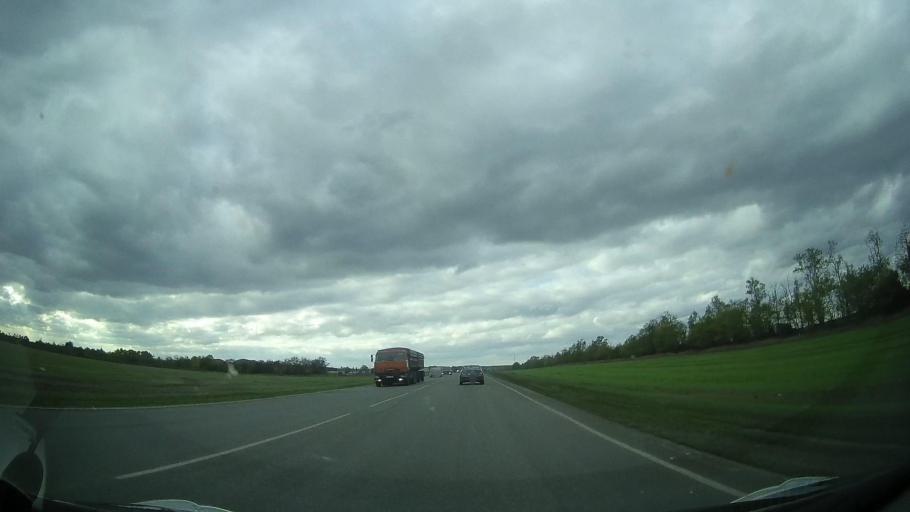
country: RU
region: Rostov
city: Kagal'nitskaya
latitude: 46.8711
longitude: 40.1670
